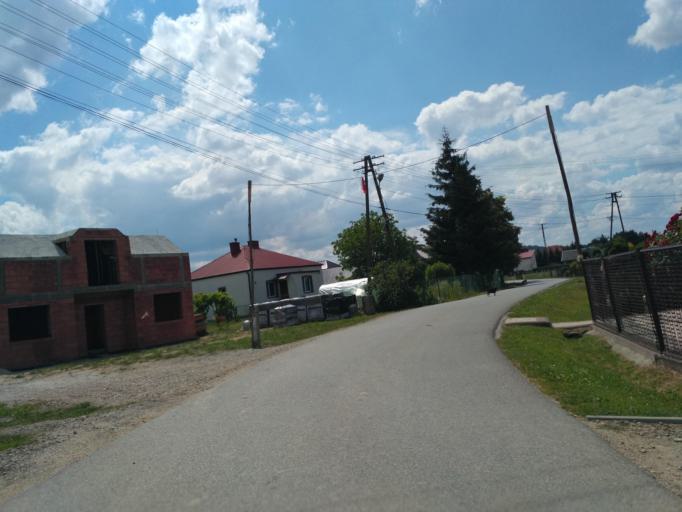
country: PL
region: Subcarpathian Voivodeship
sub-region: Powiat jasielski
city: Kolaczyce
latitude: 49.8117
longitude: 21.4144
